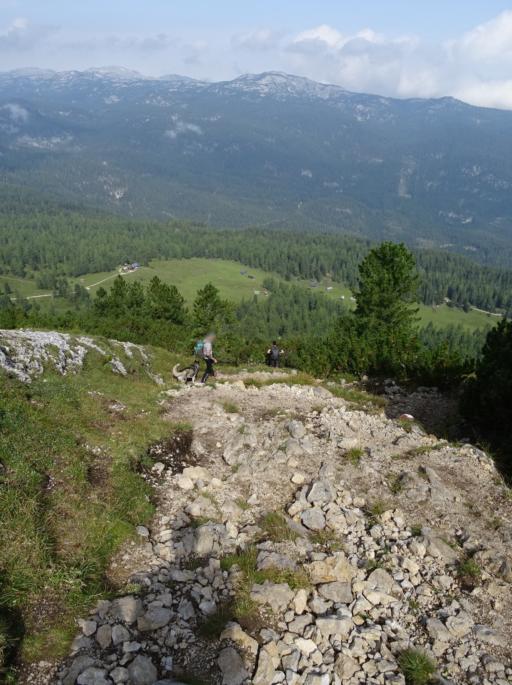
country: AT
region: Styria
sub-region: Politischer Bezirk Liezen
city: Aich
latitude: 47.4593
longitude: 13.8252
